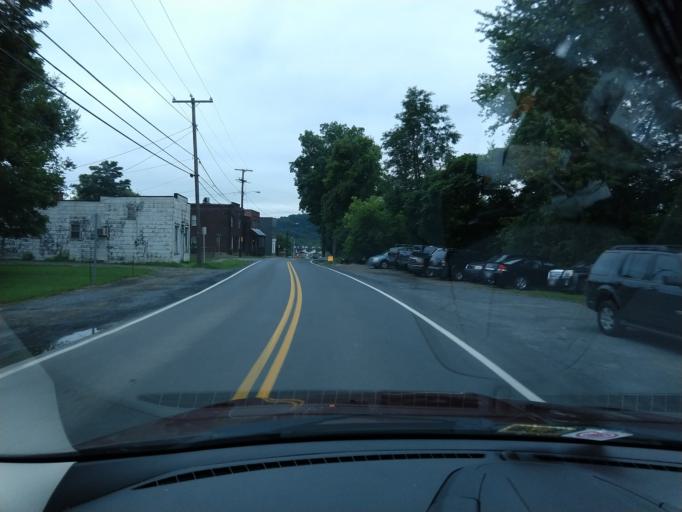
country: US
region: Virginia
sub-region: City of Covington
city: Fairlawn
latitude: 37.7604
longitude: -79.9947
